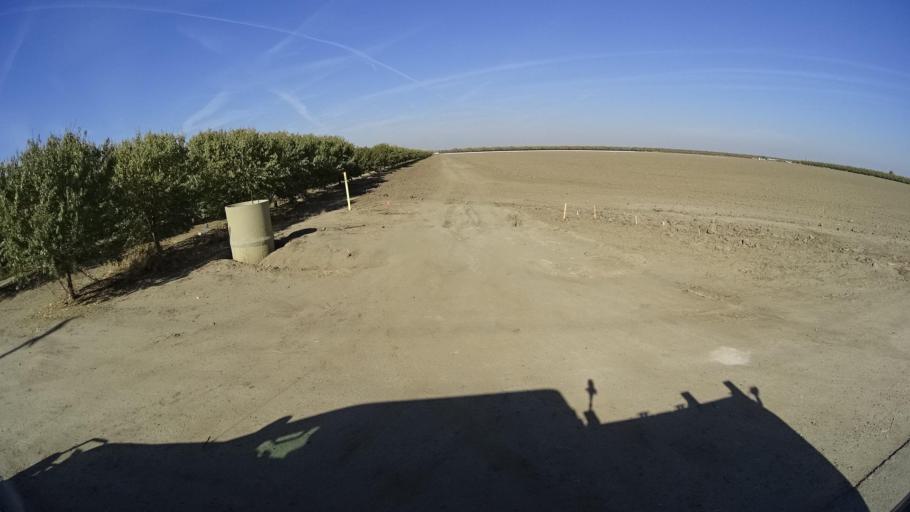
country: US
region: California
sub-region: Kern County
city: Wasco
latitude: 35.6670
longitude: -119.3795
